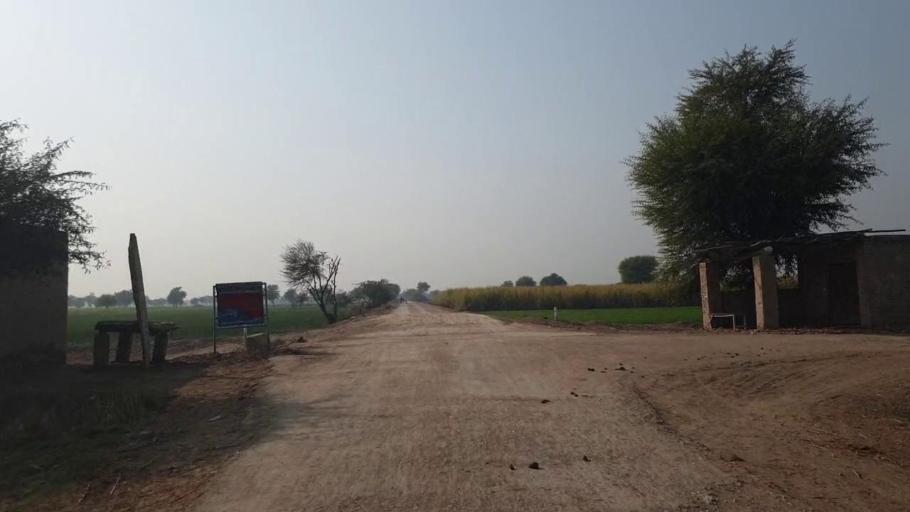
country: PK
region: Sindh
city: Shahdadpur
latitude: 26.0005
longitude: 68.5461
